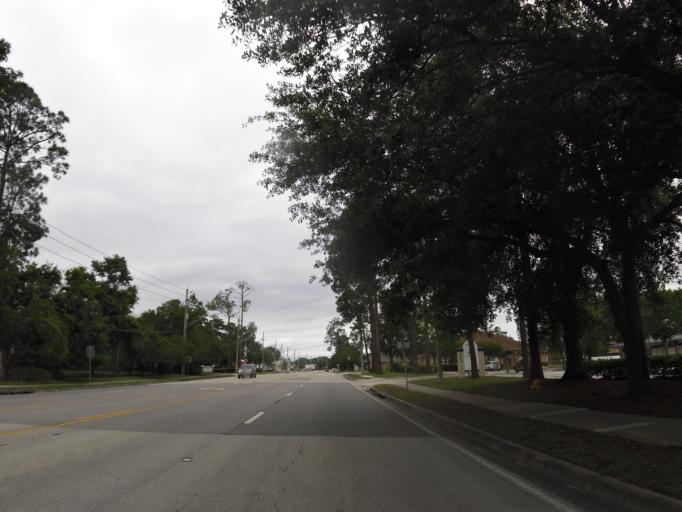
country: US
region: Florida
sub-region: Saint Johns County
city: Fruit Cove
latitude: 30.1983
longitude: -81.6141
